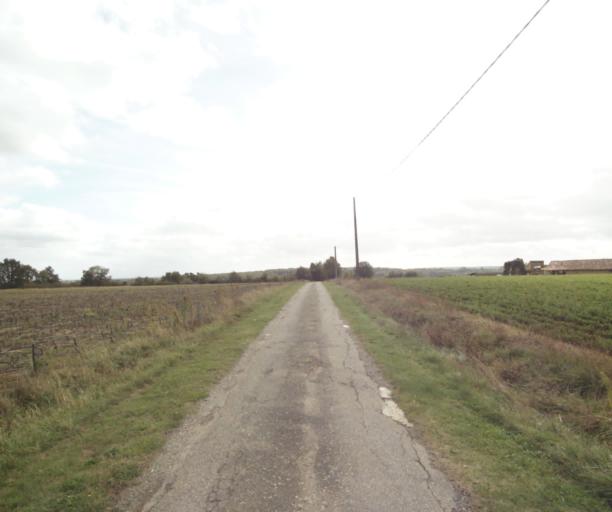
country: FR
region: Midi-Pyrenees
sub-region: Departement du Tarn-et-Garonne
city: Finhan
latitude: 43.8845
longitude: 1.1335
